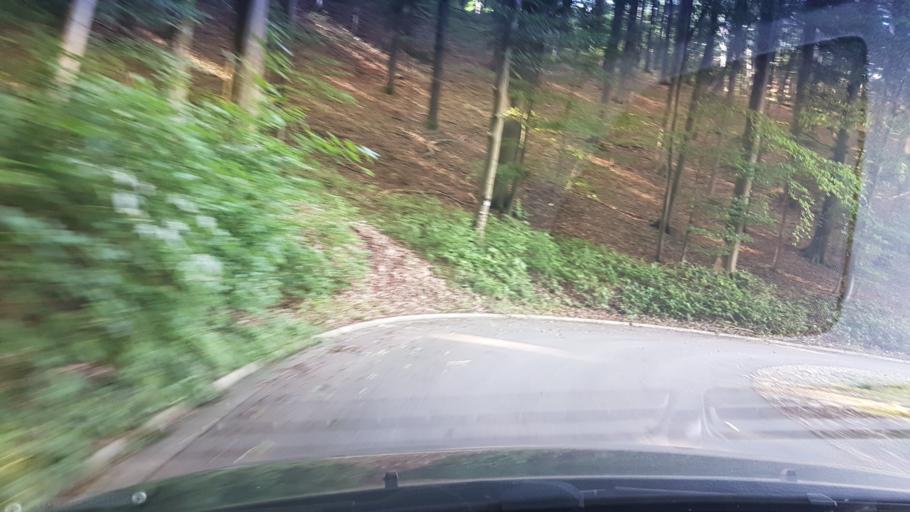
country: DE
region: Bavaria
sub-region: Upper Franconia
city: Schesslitz
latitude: 49.9904
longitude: 11.0757
